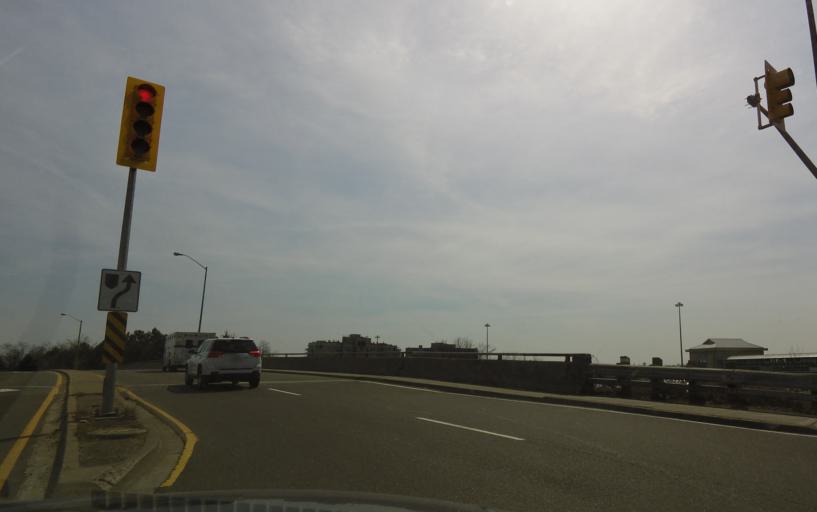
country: CA
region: Ontario
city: Oshawa
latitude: 43.8648
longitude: -78.9359
